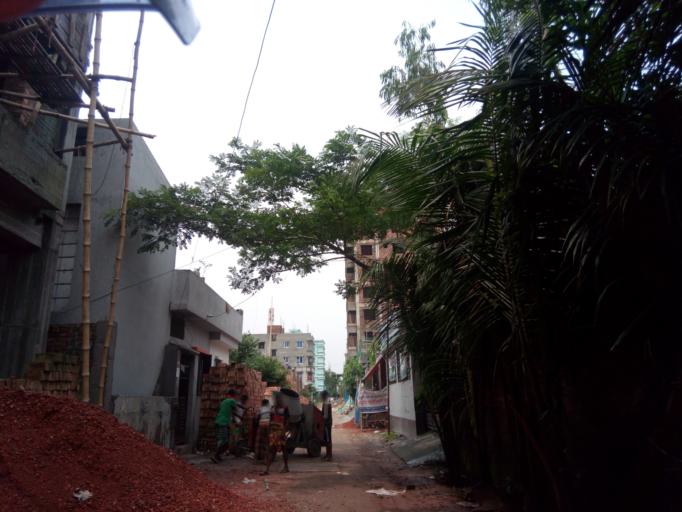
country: BD
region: Dhaka
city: Azimpur
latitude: 23.7445
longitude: 90.3500
